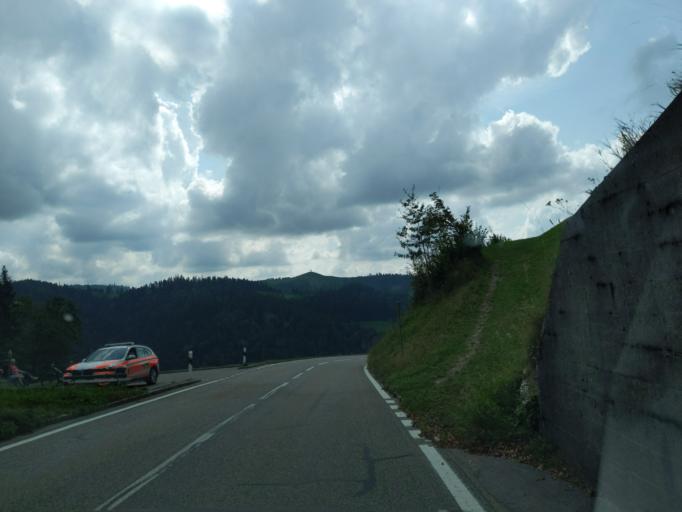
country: CH
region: Bern
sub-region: Oberaargau
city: Wyssachen
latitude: 47.0553
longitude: 7.8360
